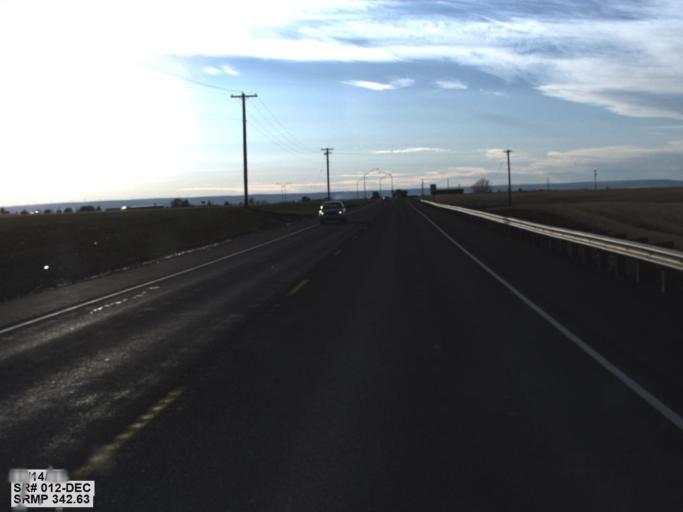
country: US
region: Washington
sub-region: Walla Walla County
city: Walla Walla East
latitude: 46.1020
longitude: -118.2461
